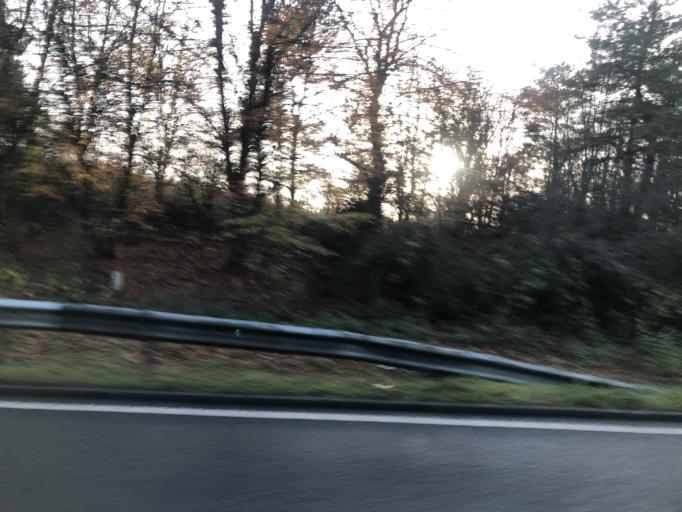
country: GB
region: England
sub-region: Surrey
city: Bletchingley
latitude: 51.2643
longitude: -0.1241
